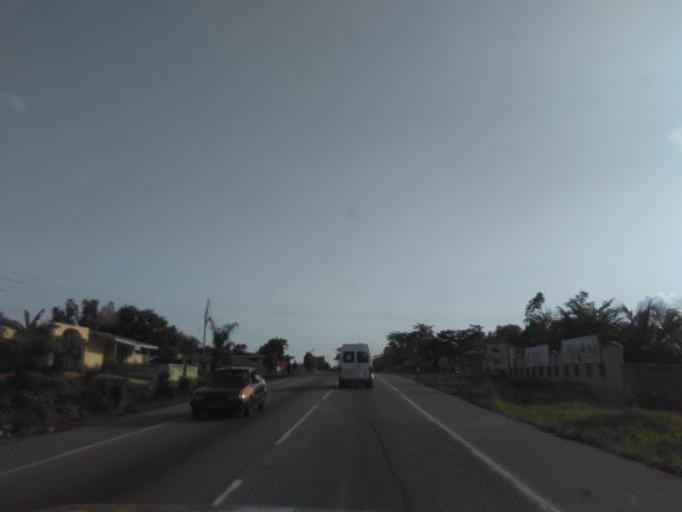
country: GH
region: Ashanti
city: Konongo
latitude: 6.6141
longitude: -1.2361
